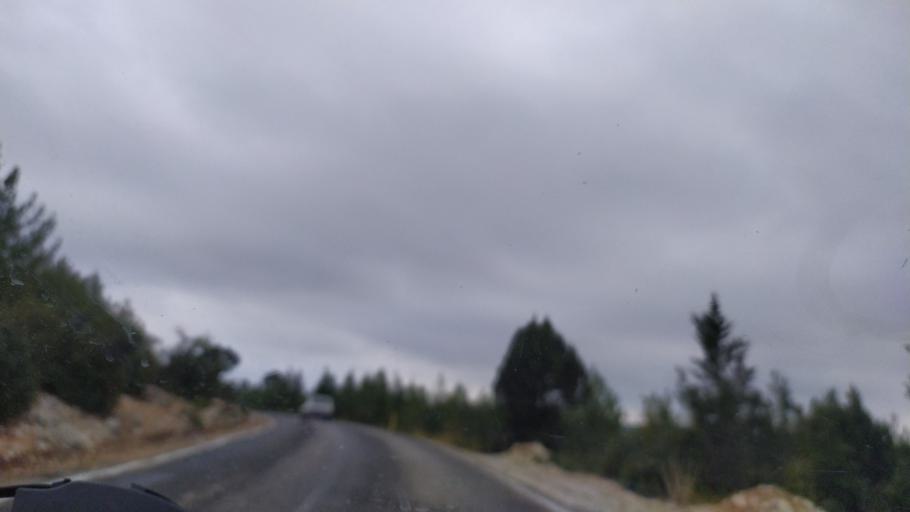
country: TR
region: Mersin
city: Silifke
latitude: 36.5430
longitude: 33.9275
